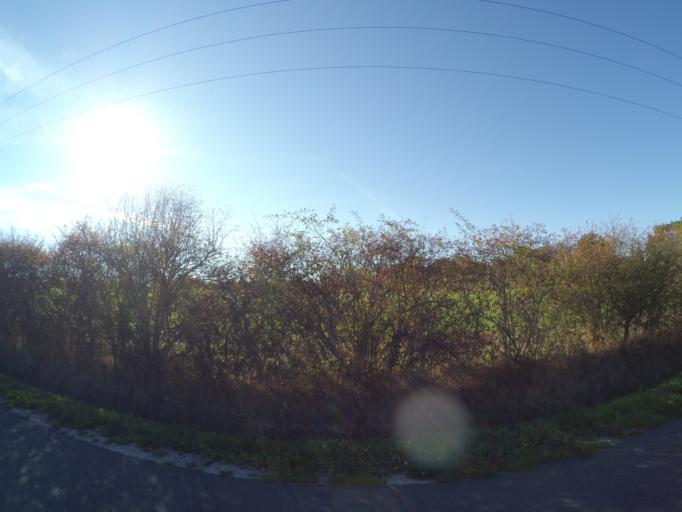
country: FR
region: Pays de la Loire
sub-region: Departement de la Loire-Atlantique
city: Saint-Lumine-de-Clisson
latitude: 47.0831
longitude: -1.3289
